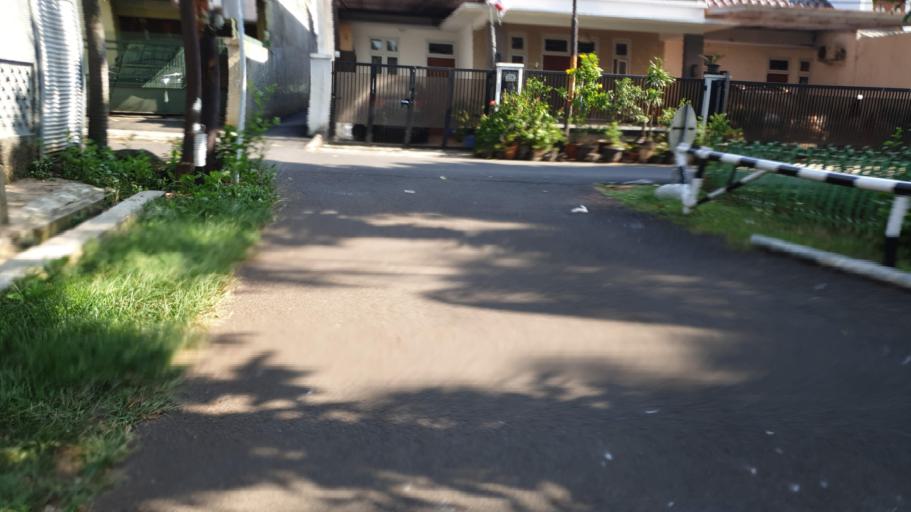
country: ID
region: Jakarta Raya
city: Jakarta
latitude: -6.2900
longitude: 106.8392
